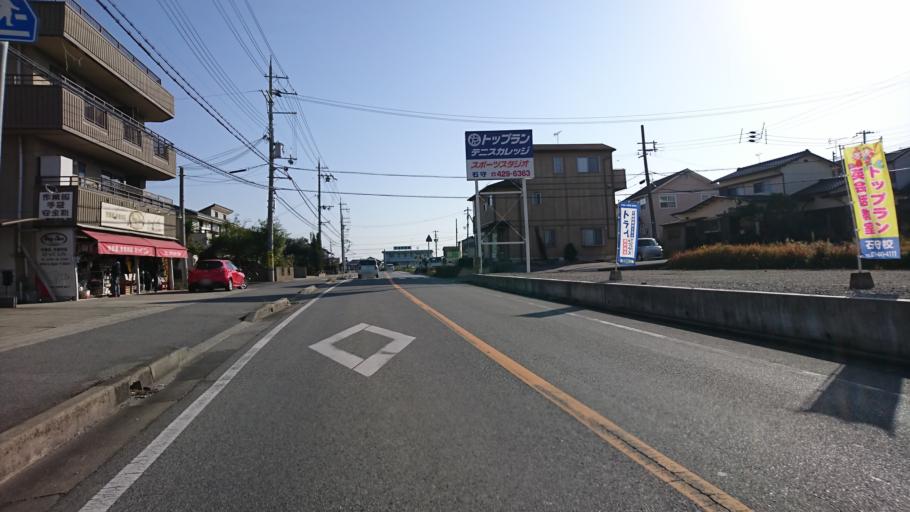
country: JP
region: Hyogo
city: Kakogawacho-honmachi
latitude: 34.7634
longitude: 134.8802
